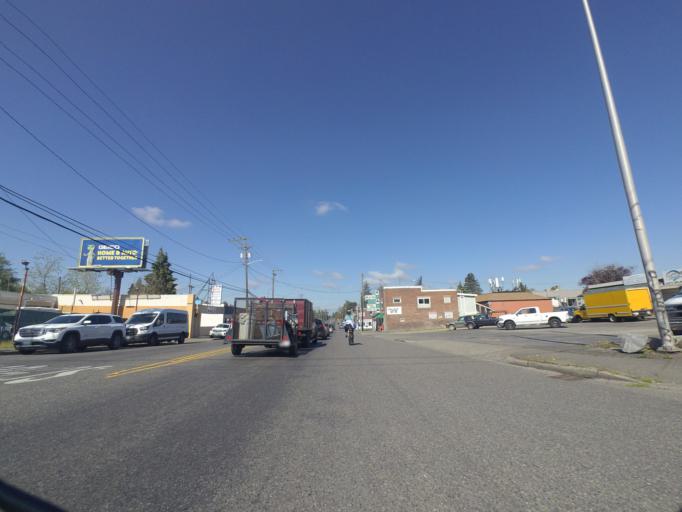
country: US
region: Washington
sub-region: Pierce County
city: Tacoma
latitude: 47.2065
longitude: -122.4498
